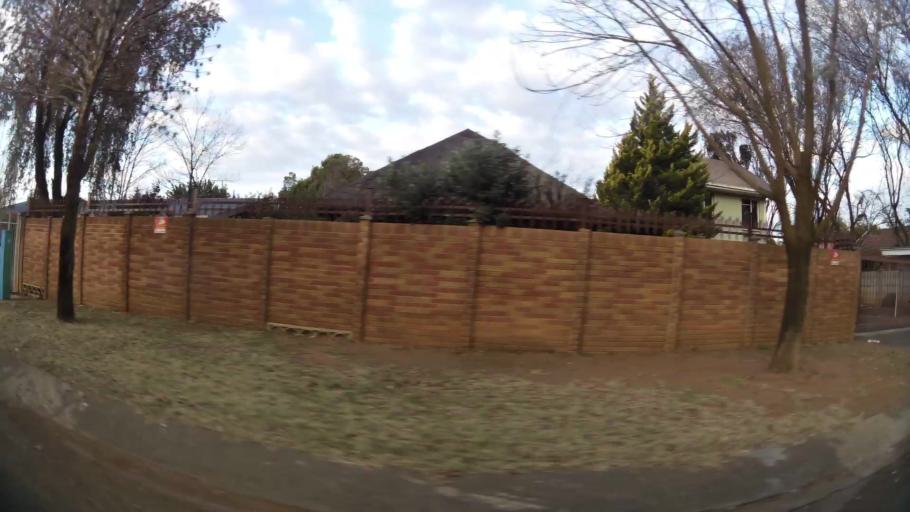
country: ZA
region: Orange Free State
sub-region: Mangaung Metropolitan Municipality
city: Bloemfontein
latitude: -29.1403
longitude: 26.1744
